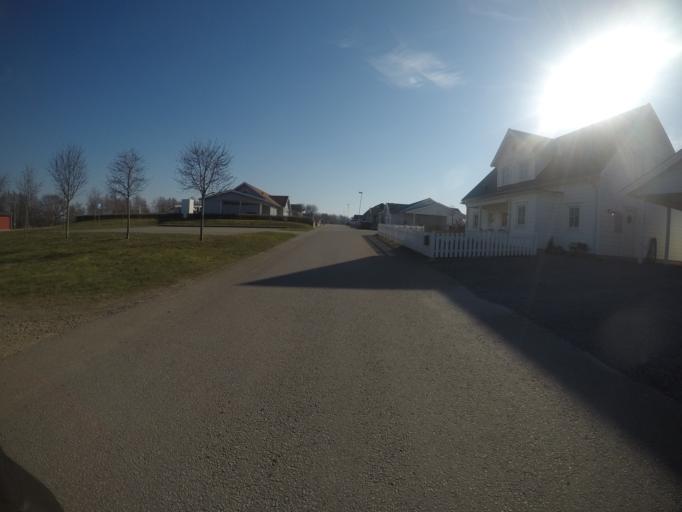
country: SE
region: Halland
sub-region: Laholms Kommun
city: Laholm
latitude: 56.5029
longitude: 13.0662
